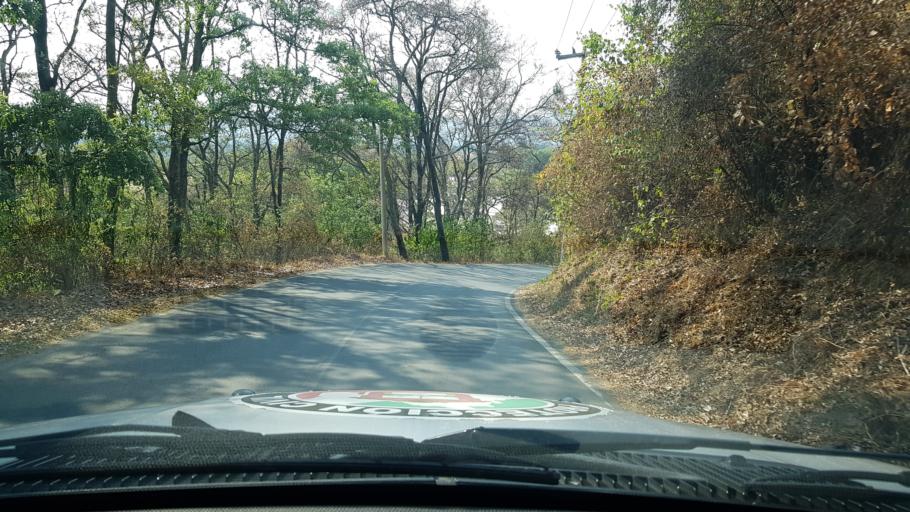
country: MX
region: Mexico
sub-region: Ozumba
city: San Jose Tlacotitlan
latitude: 18.9878
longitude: -98.8187
